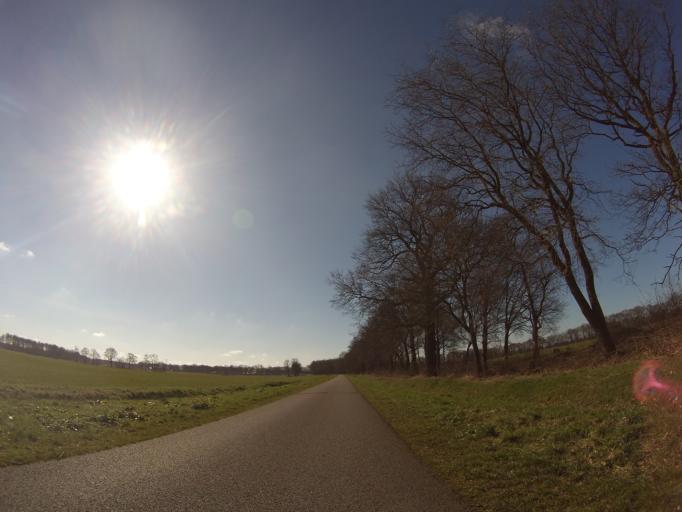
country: NL
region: Drenthe
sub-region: Gemeente Coevorden
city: Sleen
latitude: 52.7678
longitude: 6.8248
